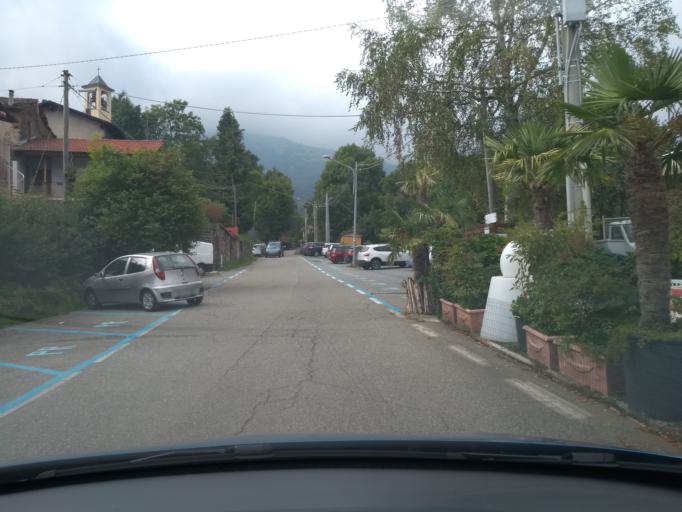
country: IT
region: Piedmont
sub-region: Provincia di Torino
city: Corio
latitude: 45.3369
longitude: 7.5182
